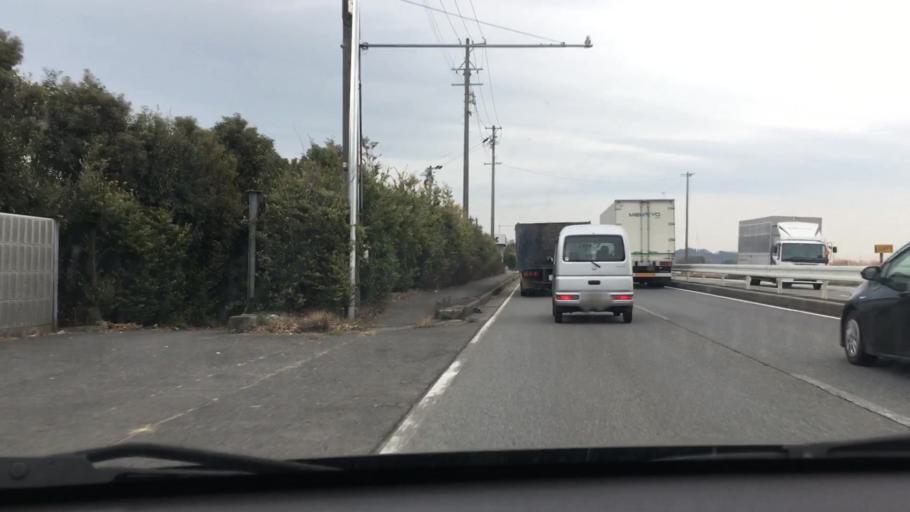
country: JP
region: Mie
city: Suzuka
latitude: 34.8840
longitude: 136.5268
